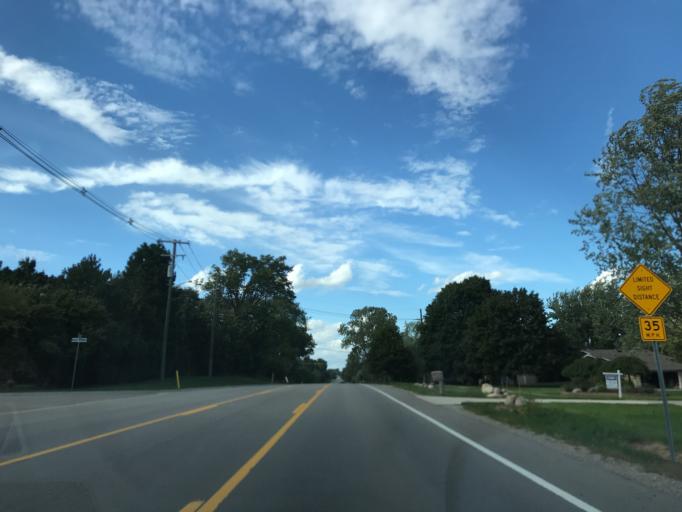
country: US
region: Michigan
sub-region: Oakland County
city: Farmington Hills
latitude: 42.5139
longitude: -83.3985
